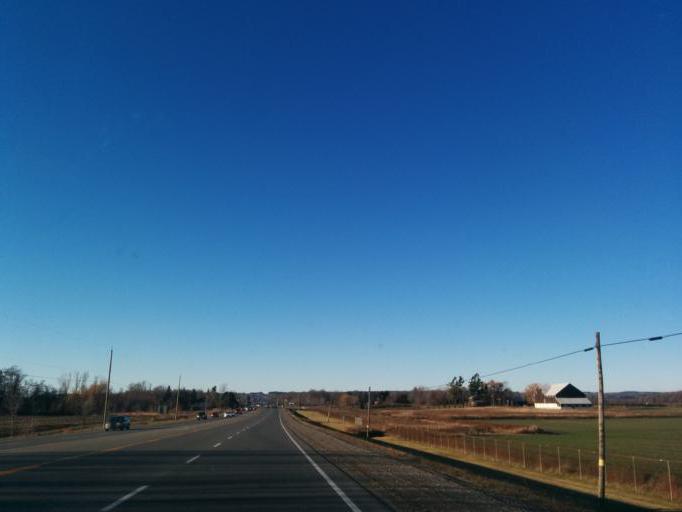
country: CA
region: Ontario
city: Brampton
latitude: 43.7971
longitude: -79.9103
